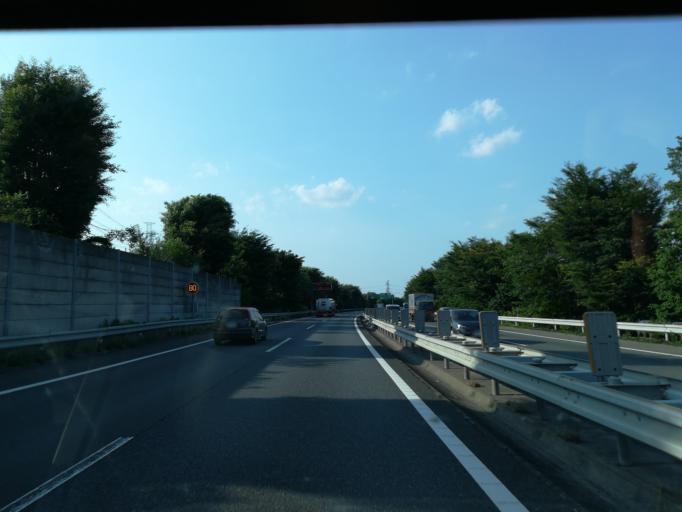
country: JP
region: Saitama
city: Sakado
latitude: 35.9145
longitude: 139.3868
